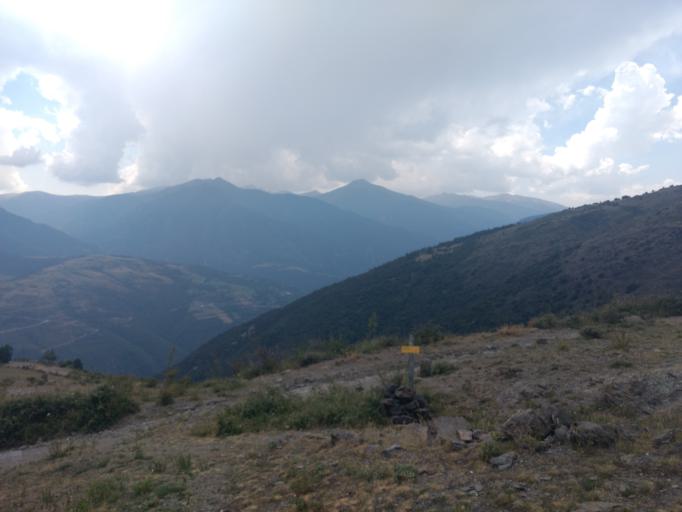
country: FR
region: Languedoc-Roussillon
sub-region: Departement des Pyrenees-Orientales
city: Vernet-les-Bains
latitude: 42.5789
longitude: 2.2873
